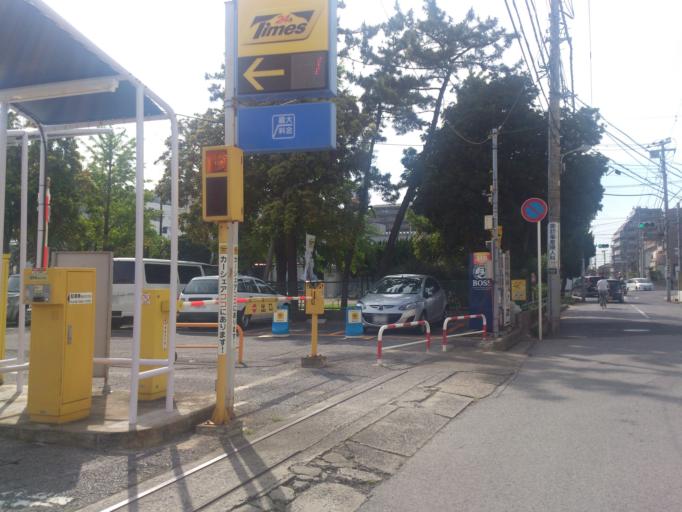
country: JP
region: Chiba
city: Funabashi
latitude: 35.6581
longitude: 140.0529
